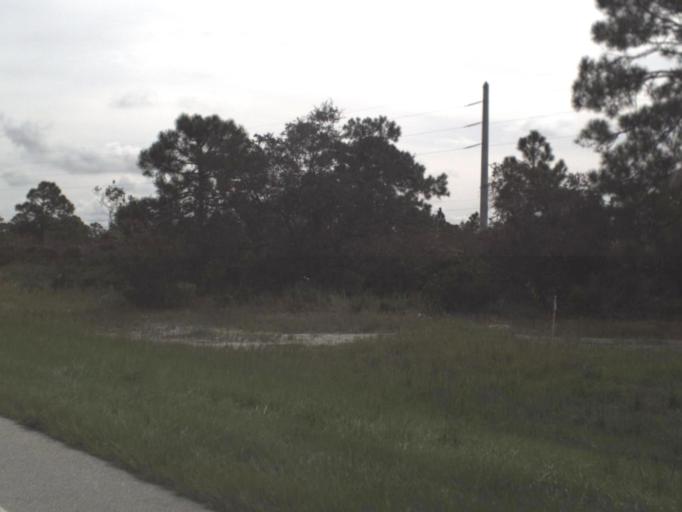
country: US
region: Florida
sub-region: Highlands County
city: Placid Lakes
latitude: 27.2092
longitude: -81.3575
